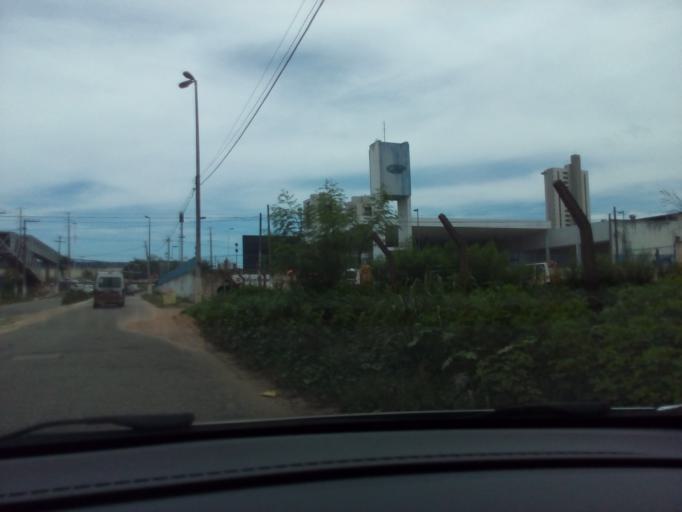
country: BR
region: Rio Grande do Norte
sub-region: Natal
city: Natal
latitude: -5.8493
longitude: -35.2106
